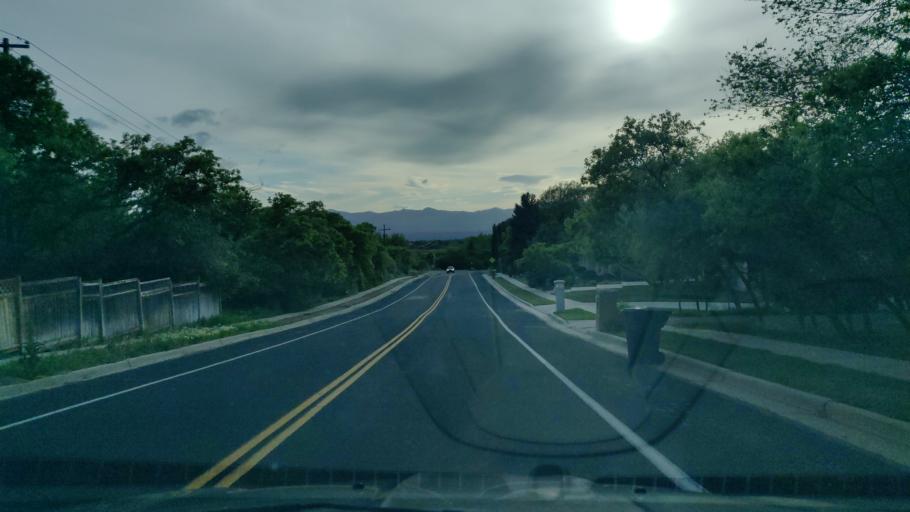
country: US
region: Utah
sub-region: Salt Lake County
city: Granite
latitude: 40.5898
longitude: -111.7958
